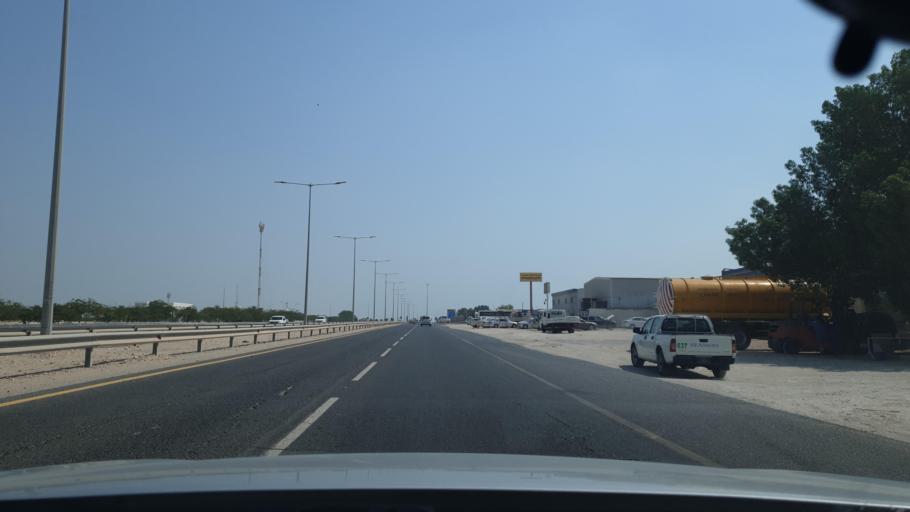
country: QA
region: Al Khawr
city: Al Khawr
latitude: 25.7171
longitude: 51.5045
